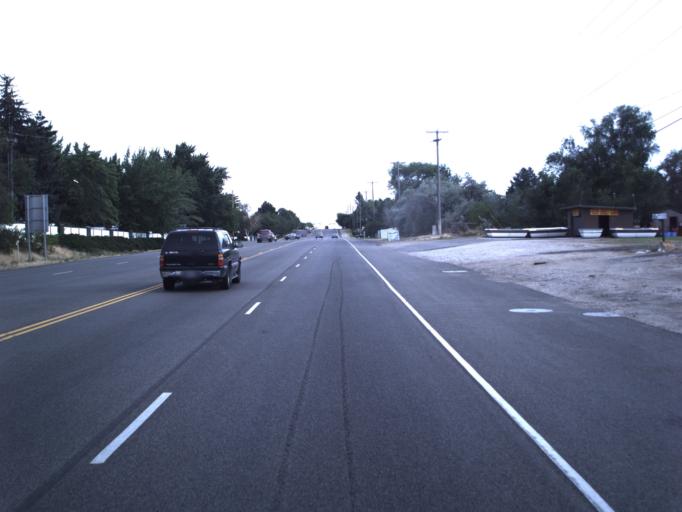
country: US
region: Utah
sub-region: Weber County
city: West Haven
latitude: 41.1971
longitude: -112.0259
